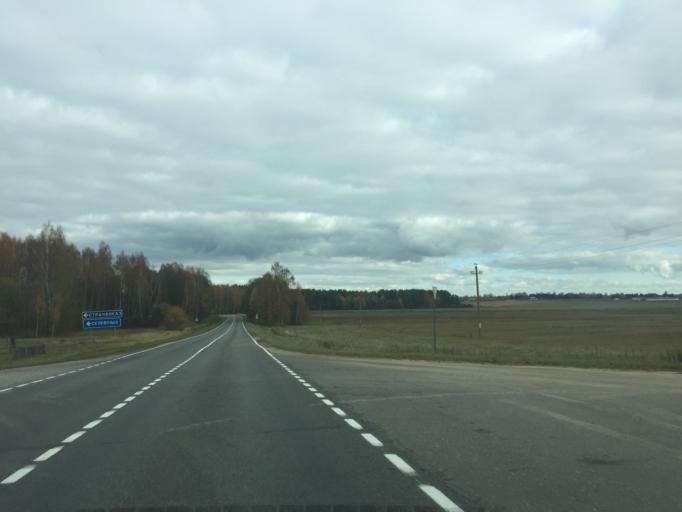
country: BY
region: Minsk
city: Svir
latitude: 54.8784
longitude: 26.3648
